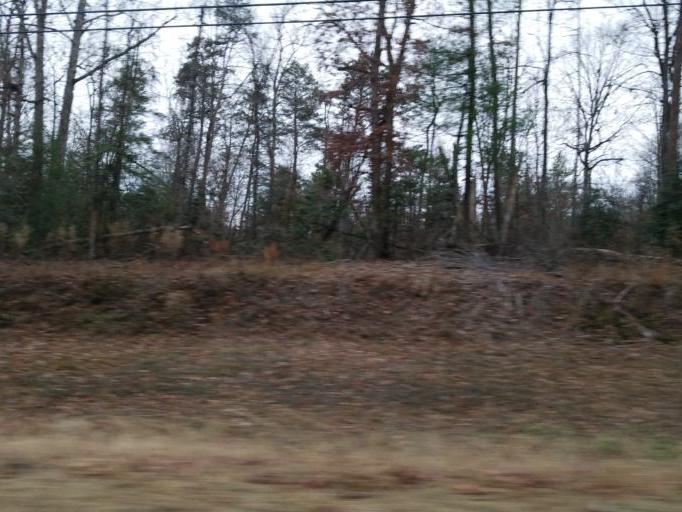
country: US
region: Georgia
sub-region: Dawson County
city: Dawsonville
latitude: 34.4995
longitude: -84.2028
